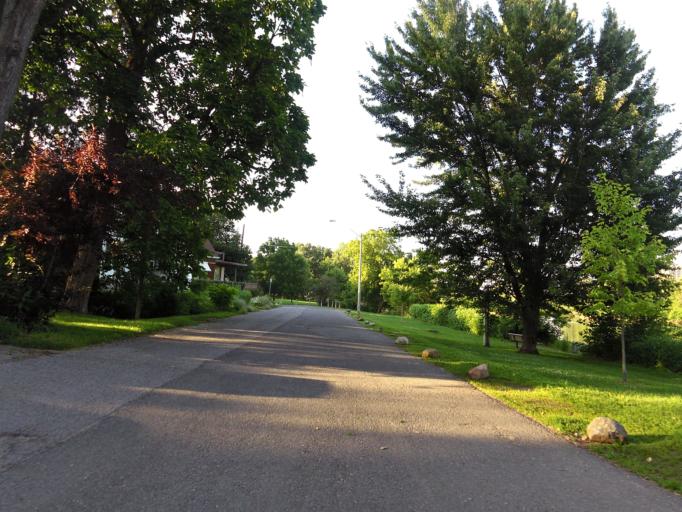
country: CA
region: Ontario
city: Ottawa
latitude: 45.3960
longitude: -75.6742
